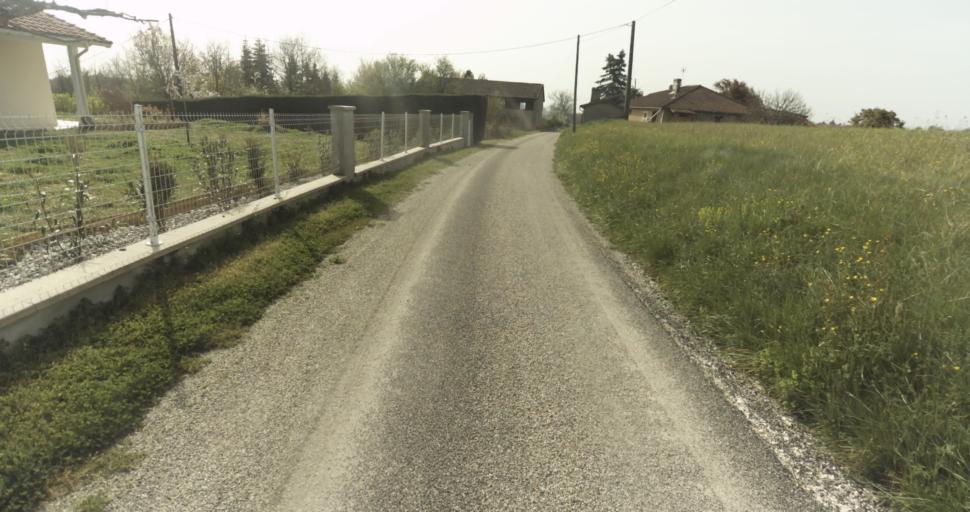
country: FR
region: Midi-Pyrenees
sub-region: Departement du Tarn-et-Garonne
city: Moissac
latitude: 44.1325
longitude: 1.0954
